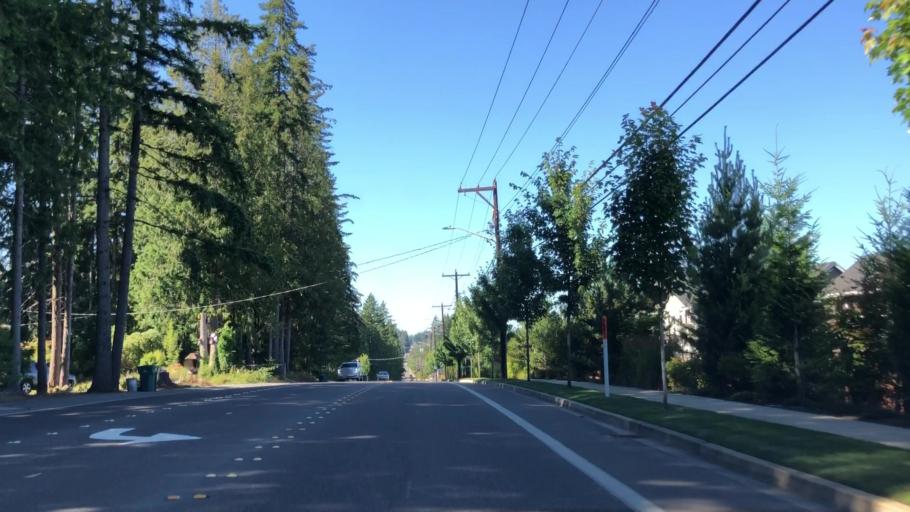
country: US
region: Washington
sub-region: Snohomish County
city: North Creek
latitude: 47.8189
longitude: -122.1860
